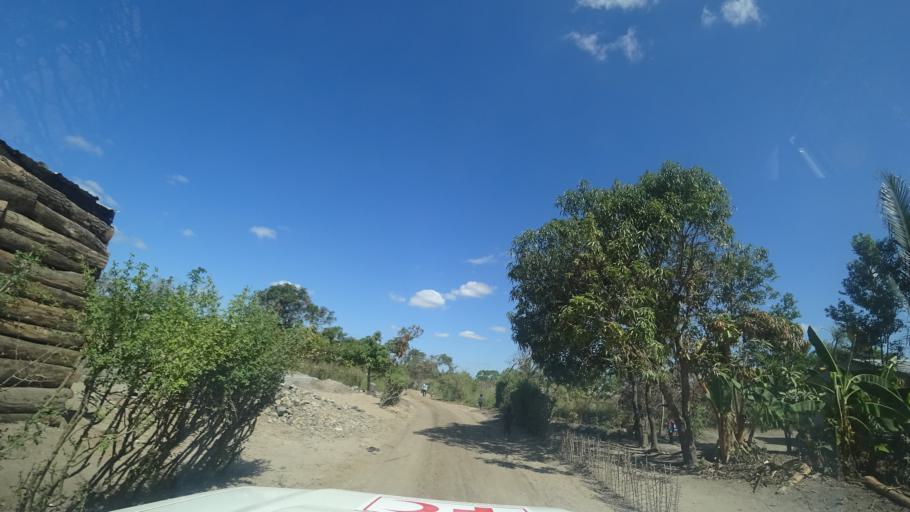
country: MZ
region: Sofala
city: Dondo
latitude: -19.4892
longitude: 34.5994
